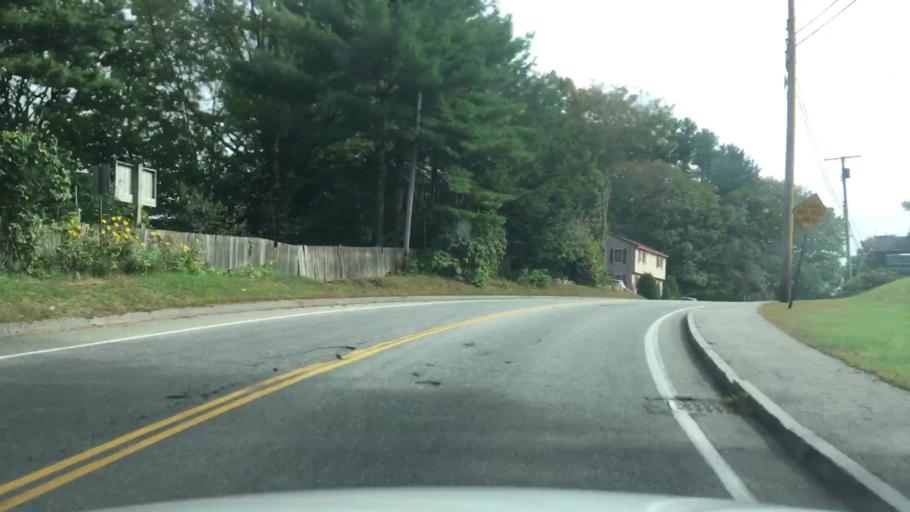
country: US
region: Maine
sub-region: Sagadahoc County
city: Topsham
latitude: 43.9151
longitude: -69.9842
